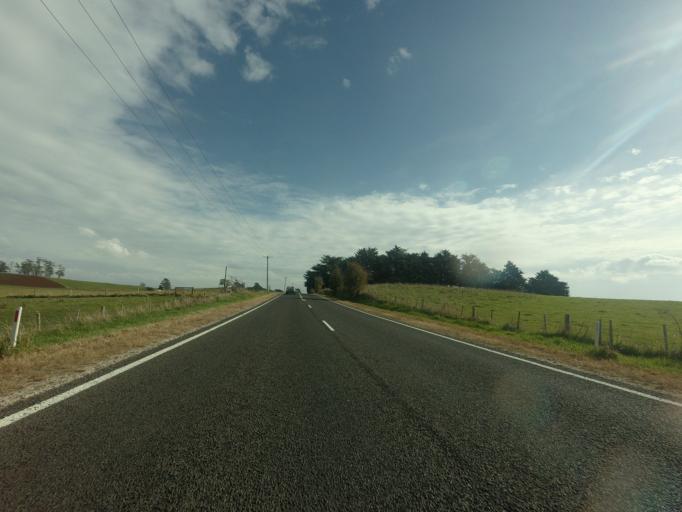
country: AU
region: Tasmania
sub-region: Meander Valley
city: Deloraine
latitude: -41.5253
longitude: 146.6993
